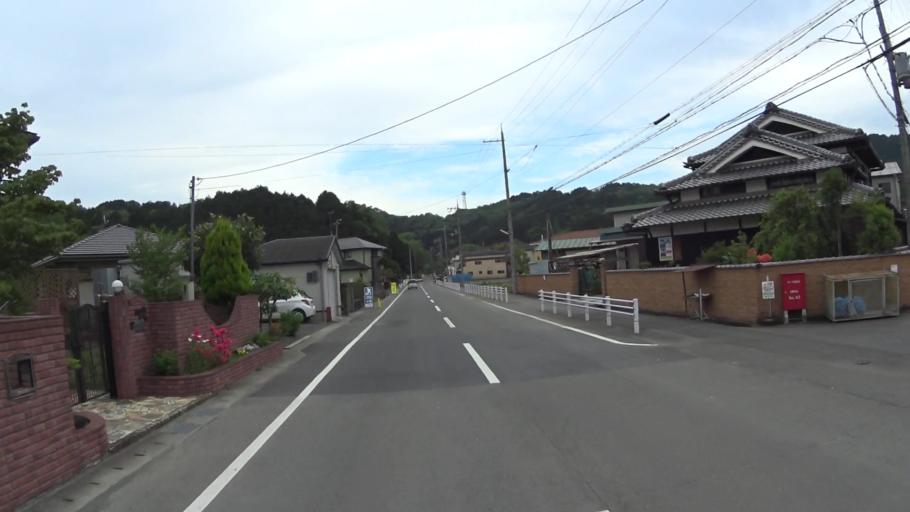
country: JP
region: Kyoto
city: Kameoka
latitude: 35.0669
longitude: 135.5332
